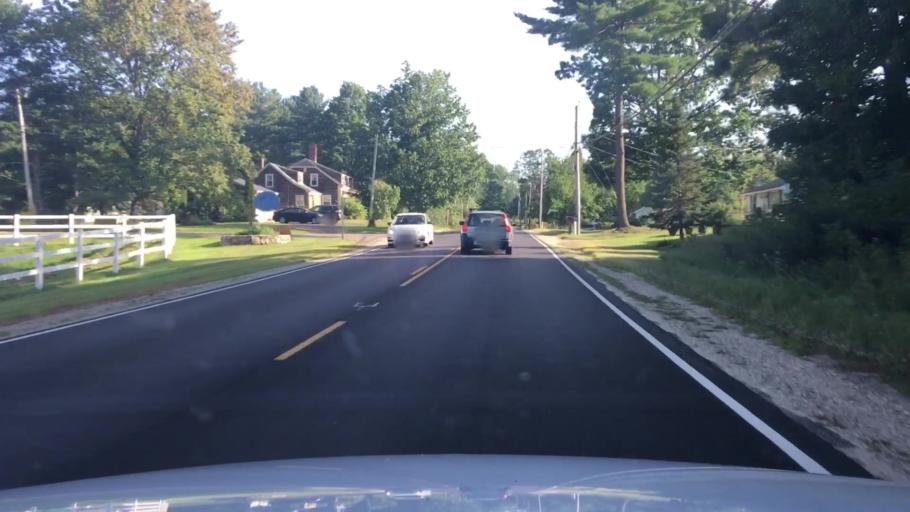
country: US
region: Maine
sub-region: Cumberland County
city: Cumberland Center
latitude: 43.7818
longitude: -70.3039
